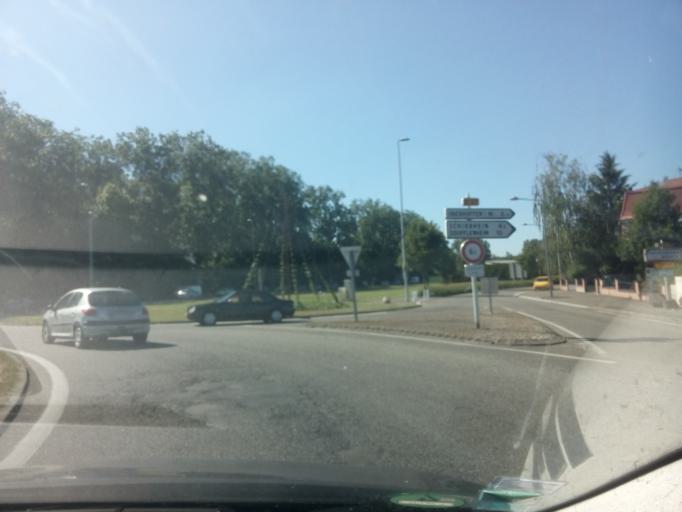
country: FR
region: Alsace
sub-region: Departement du Bas-Rhin
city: Oberhoffen-sur-Moder
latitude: 48.7711
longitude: 7.8691
